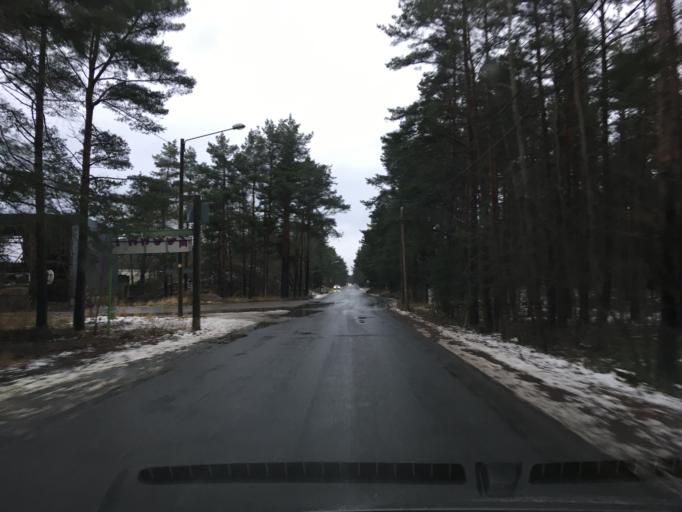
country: EE
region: Harju
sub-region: Tallinna linn
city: Tallinn
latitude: 59.3846
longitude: 24.7282
